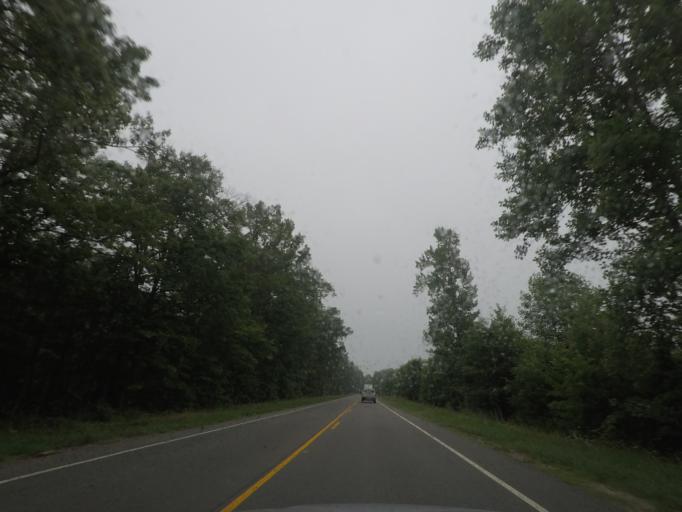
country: US
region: Virginia
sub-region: Buckingham County
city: Buckingham
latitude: 37.4971
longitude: -78.4762
